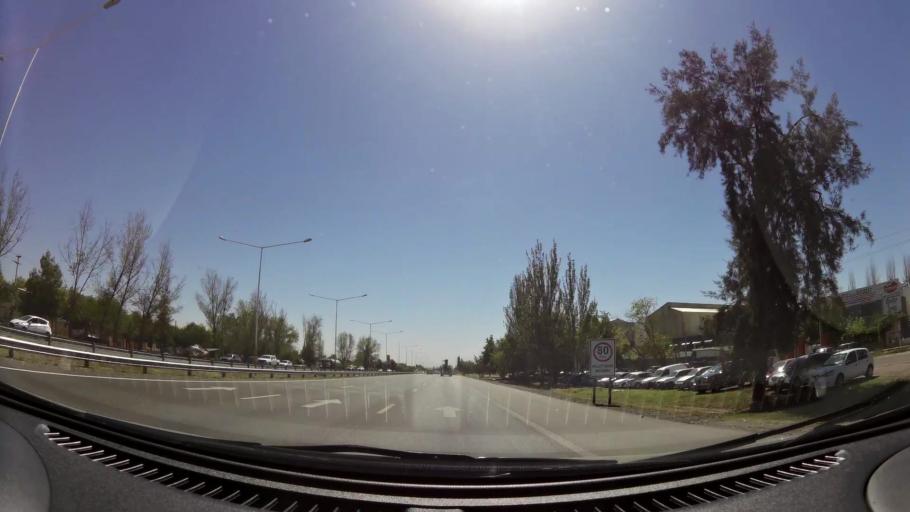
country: AR
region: Mendoza
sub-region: Departamento de Godoy Cruz
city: Godoy Cruz
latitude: -32.9620
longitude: -68.8387
